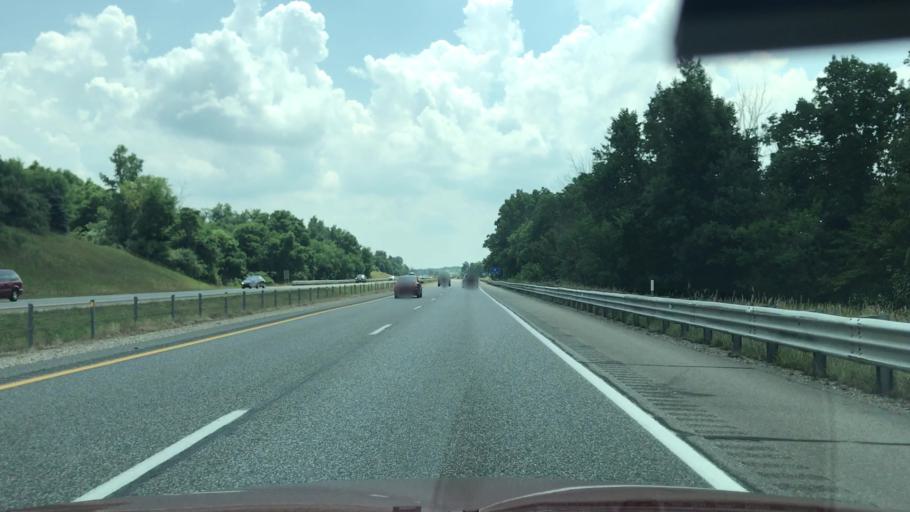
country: US
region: Michigan
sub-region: Allegan County
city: Otsego
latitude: 42.5538
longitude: -85.6623
